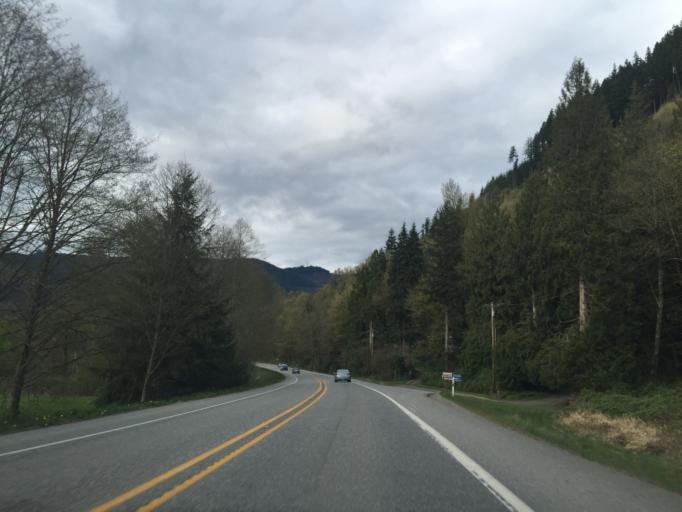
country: US
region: Washington
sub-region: Snohomish County
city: Arlington Heights
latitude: 48.2576
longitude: -122.0252
